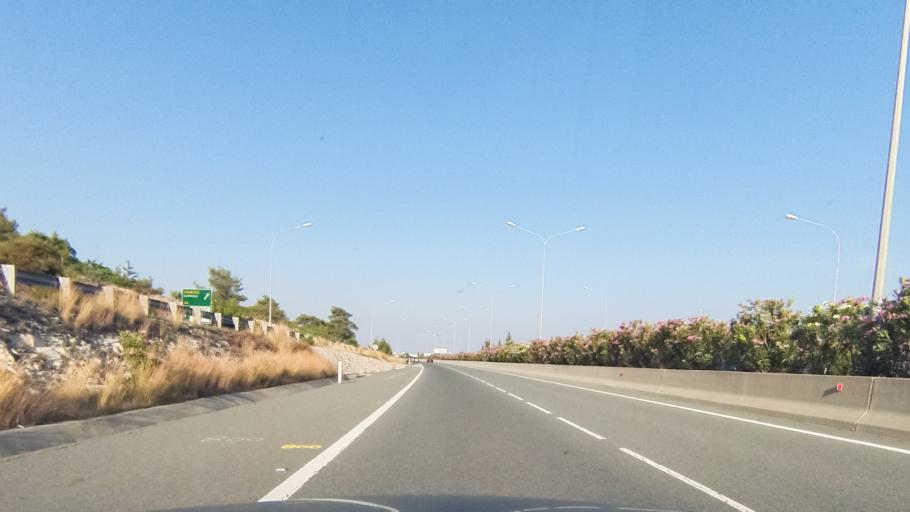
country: CY
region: Limassol
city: Erimi
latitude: 34.6812
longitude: 32.8886
